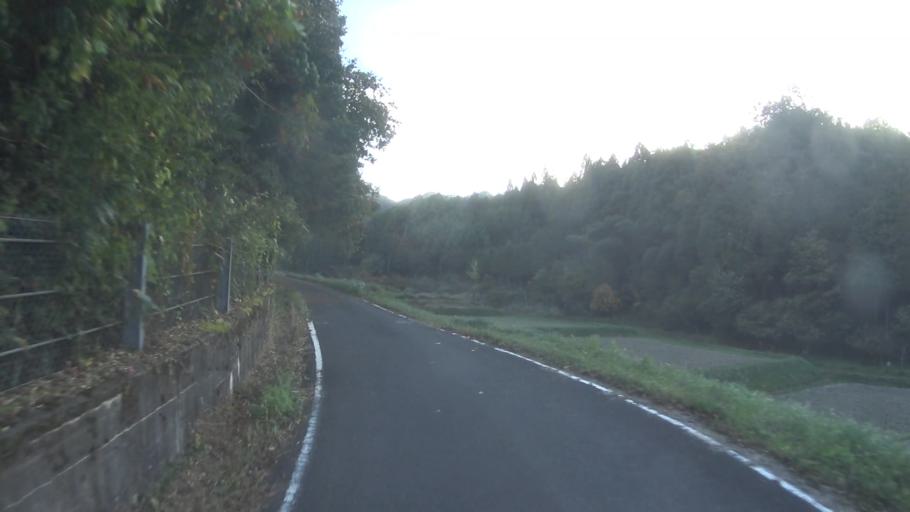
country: JP
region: Kyoto
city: Ayabe
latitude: 35.2773
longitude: 135.2496
